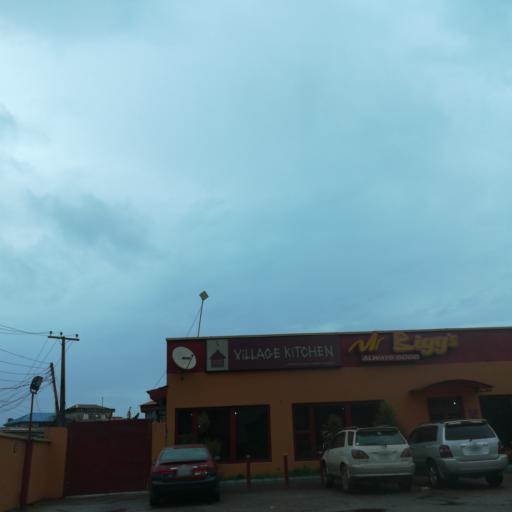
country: NG
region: Lagos
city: Oshodi
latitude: 6.5555
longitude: 3.3445
